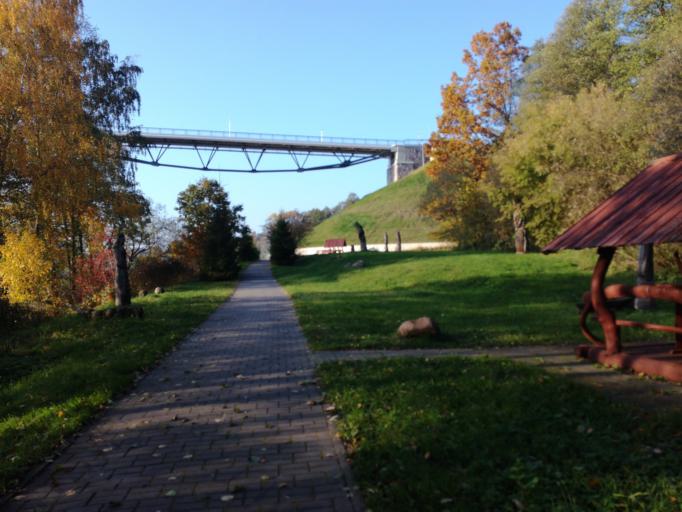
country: LT
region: Alytaus apskritis
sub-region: Alytus
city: Alytus
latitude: 54.3929
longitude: 24.0836
